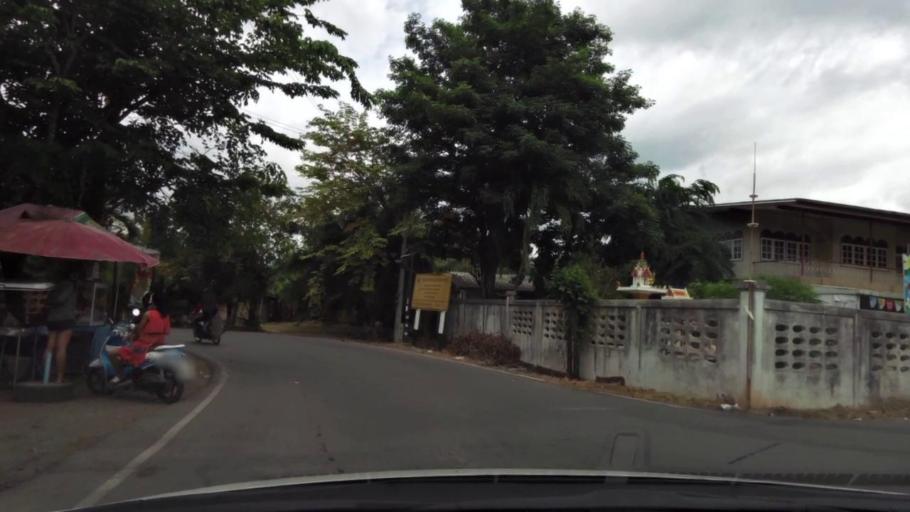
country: TH
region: Ratchaburi
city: Damnoen Saduak
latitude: 13.5755
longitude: 100.0023
